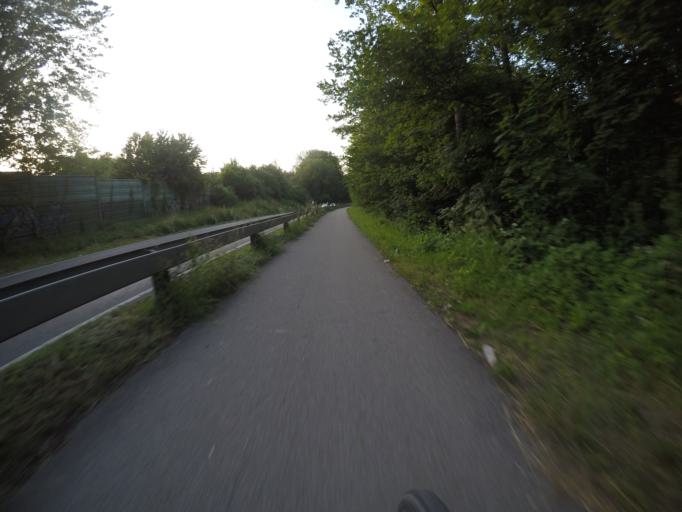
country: DE
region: Baden-Wuerttemberg
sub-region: Regierungsbezirk Stuttgart
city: Steinenbronn
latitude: 48.6704
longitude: 9.1268
